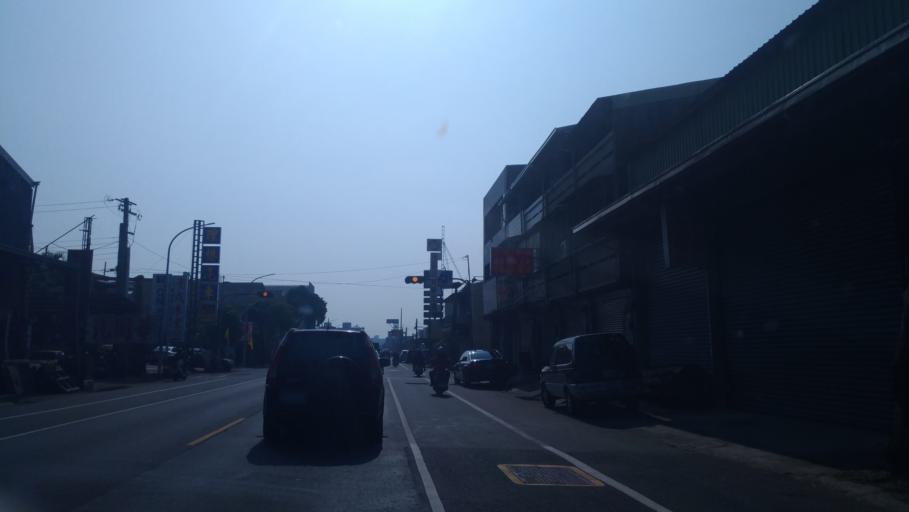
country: TW
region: Taiwan
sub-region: Chiayi
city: Jiayi Shi
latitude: 23.5017
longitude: 120.4398
